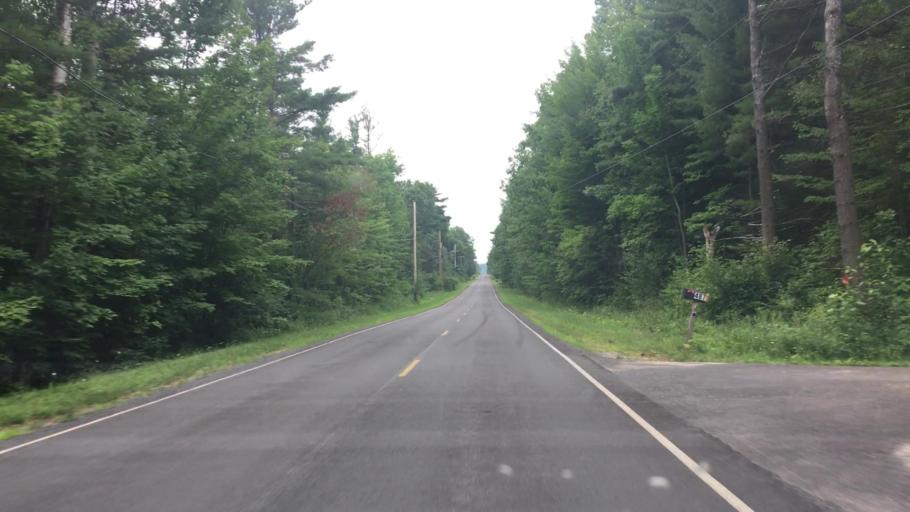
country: US
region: New York
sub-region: Clinton County
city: Peru
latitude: 44.5956
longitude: -73.6272
